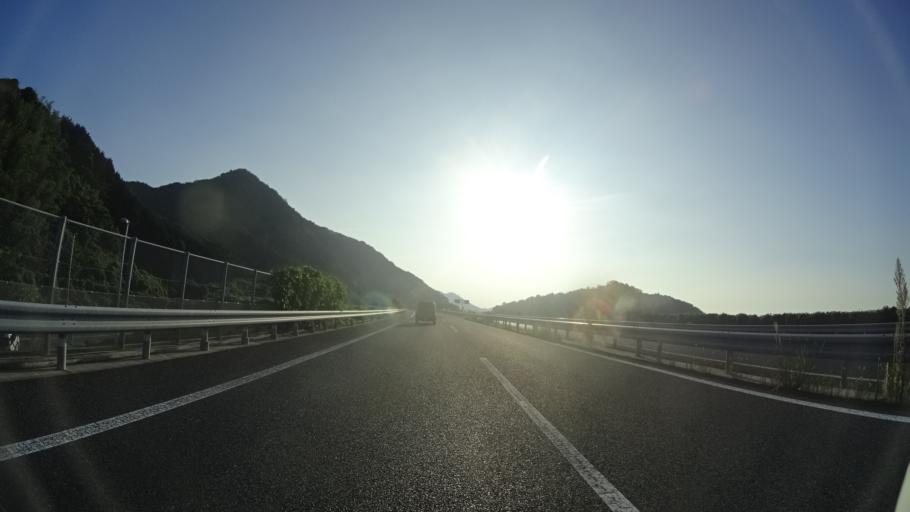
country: JP
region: Yamaguchi
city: Hagi
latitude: 34.3886
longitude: 131.3243
